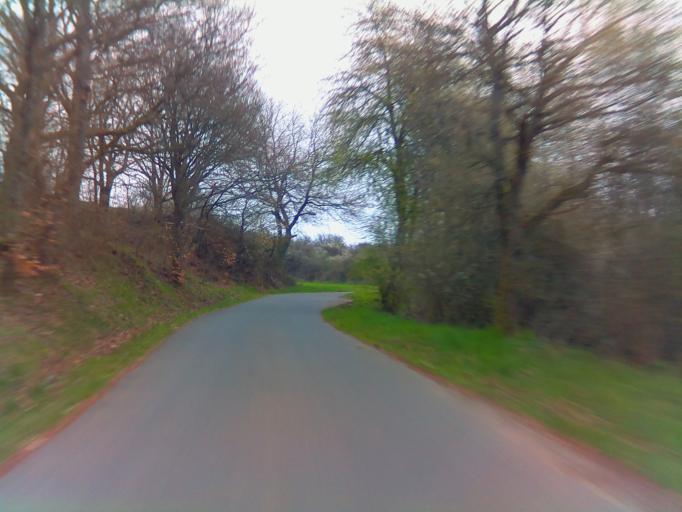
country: DE
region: Rheinland-Pfalz
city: Hoppstadten-Weiersbach
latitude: 49.6209
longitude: 7.2057
